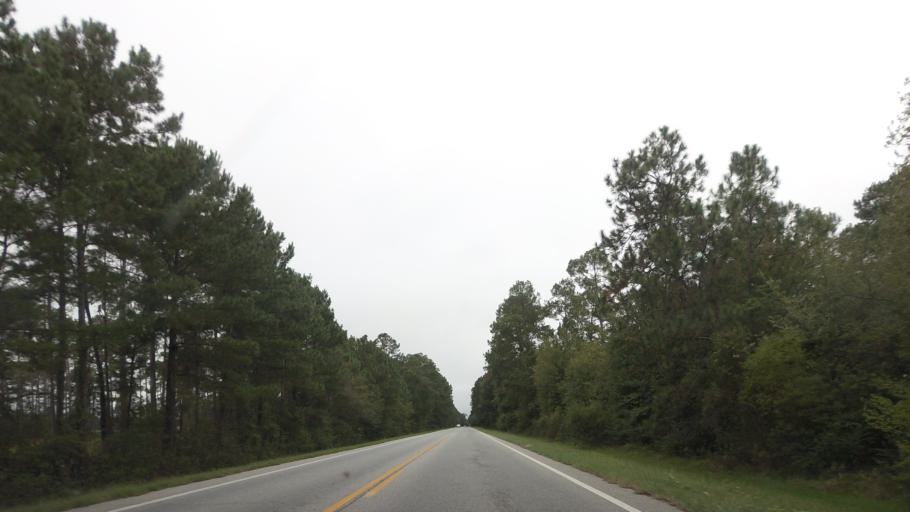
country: US
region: Georgia
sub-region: Berrien County
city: Nashville
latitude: 31.1849
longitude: -83.2427
